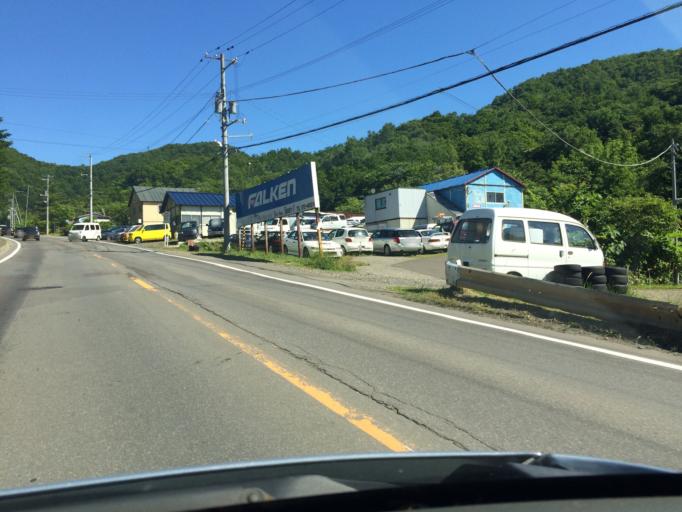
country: JP
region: Hokkaido
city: Sapporo
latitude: 43.0149
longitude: 141.3020
